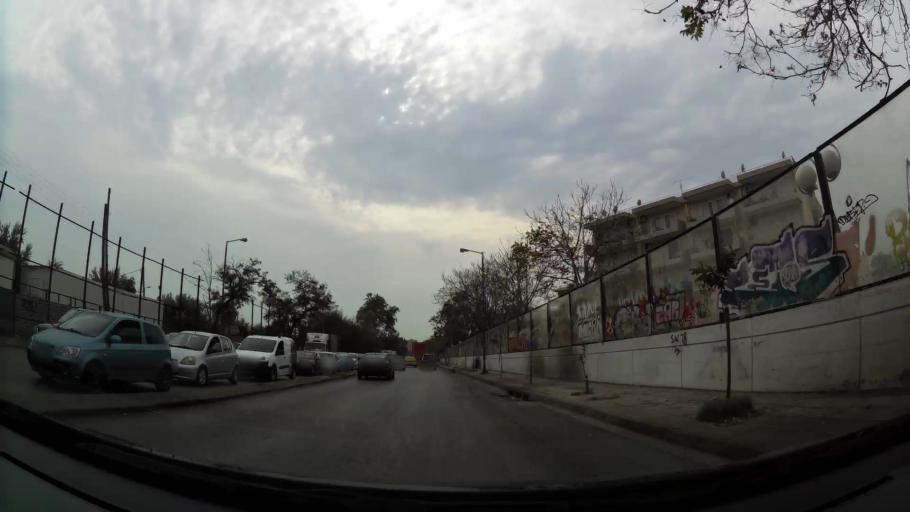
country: GR
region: Attica
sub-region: Nomarchia Athinas
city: Tavros
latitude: 37.9743
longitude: 23.7034
